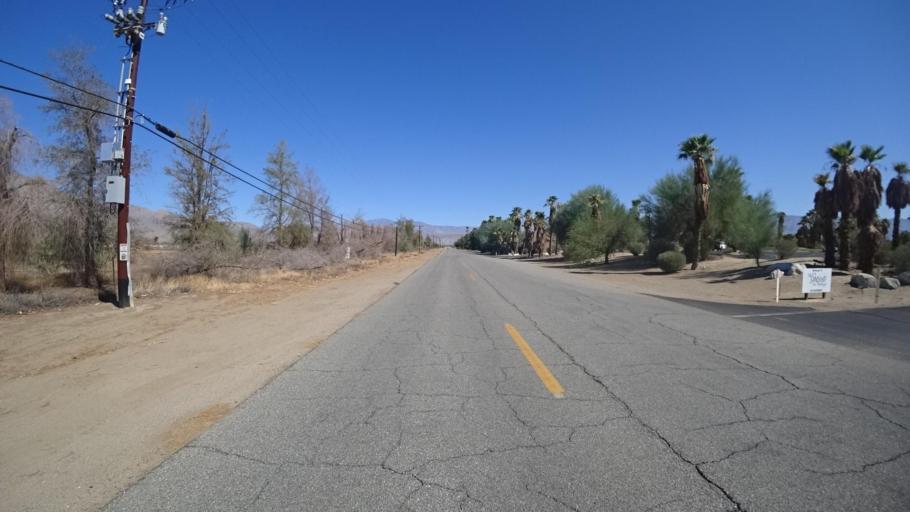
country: US
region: California
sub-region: San Diego County
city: Borrego Springs
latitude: 33.2658
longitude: -116.3660
